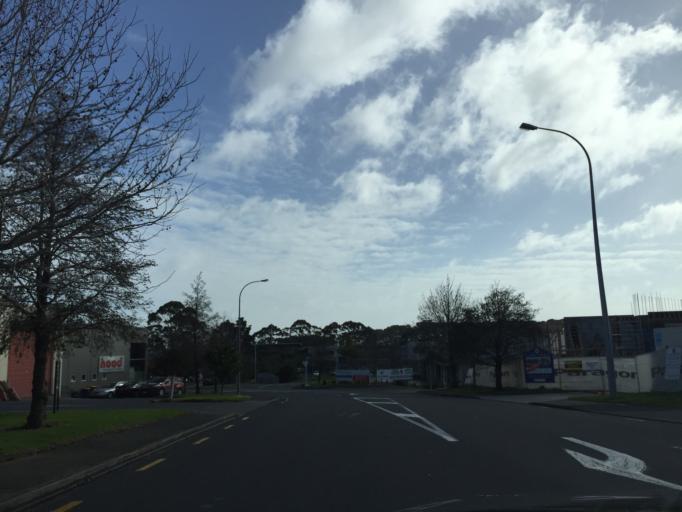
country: NZ
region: Auckland
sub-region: Auckland
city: Rothesay Bay
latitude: -36.7497
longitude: 174.7286
